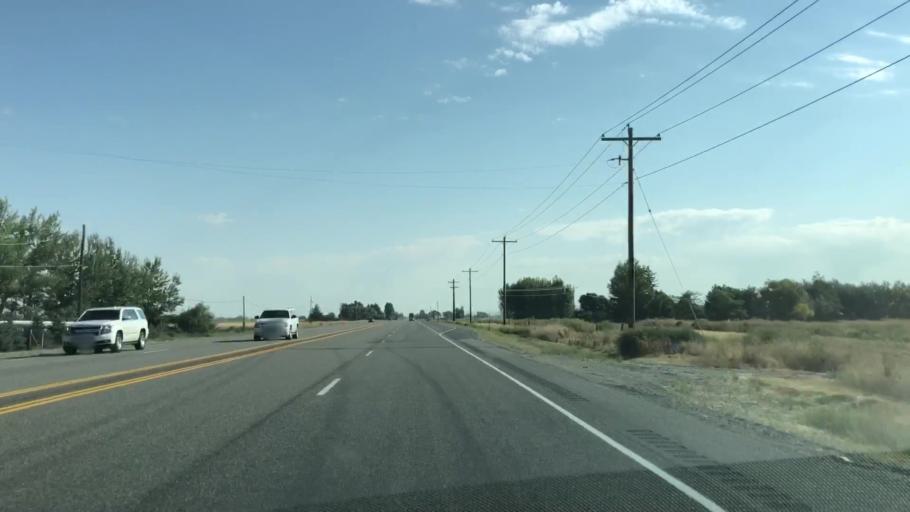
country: US
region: Idaho
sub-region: Bonneville County
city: Iona
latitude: 43.5677
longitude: -111.9199
